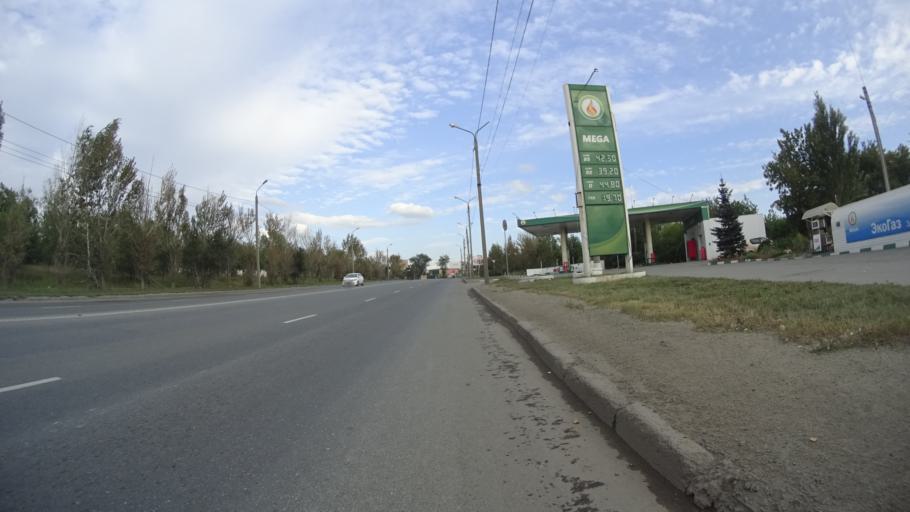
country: RU
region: Chelyabinsk
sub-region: Gorod Chelyabinsk
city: Chelyabinsk
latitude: 55.1927
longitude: 61.4213
